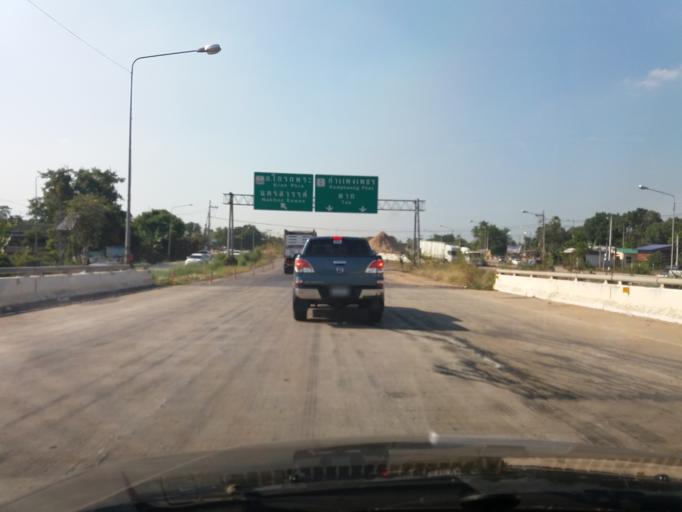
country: TH
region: Nakhon Sawan
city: Nakhon Sawan
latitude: 15.6352
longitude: 100.0989
